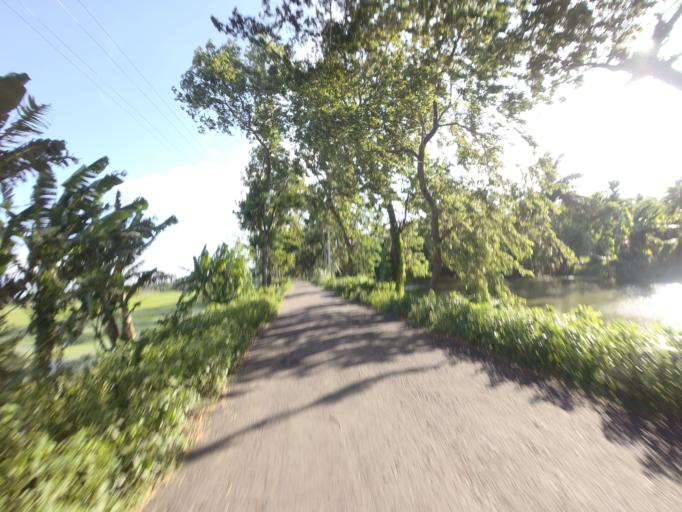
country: BD
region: Khulna
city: Kalia
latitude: 22.9571
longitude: 89.5531
